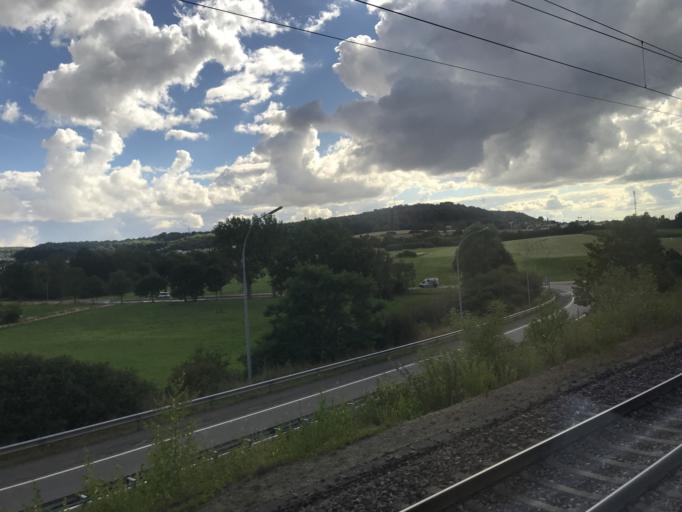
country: LU
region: Luxembourg
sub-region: Canton de Capellen
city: Bascharage
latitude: 49.5553
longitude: 5.9003
